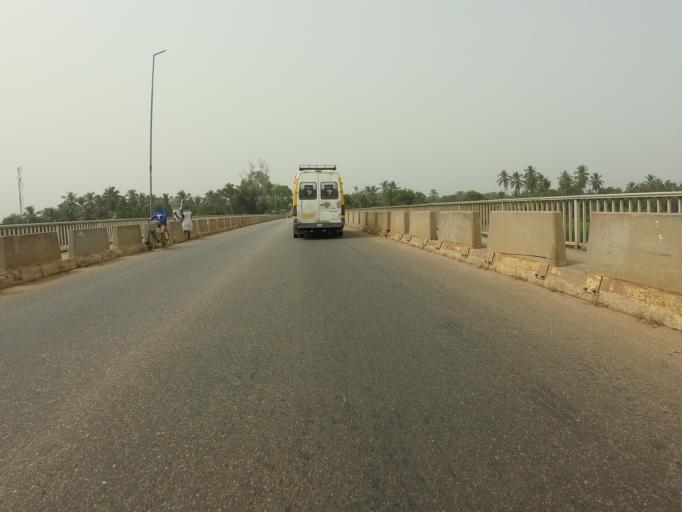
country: GH
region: Volta
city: Anloga
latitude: 5.9940
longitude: 0.5833
